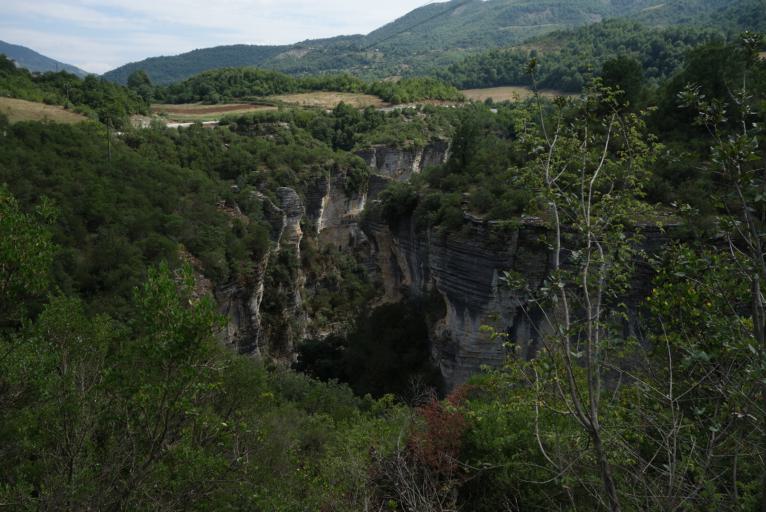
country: AL
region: Berat
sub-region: Rrethi i Skraparit
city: Cepan
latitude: 40.4369
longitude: 20.2835
